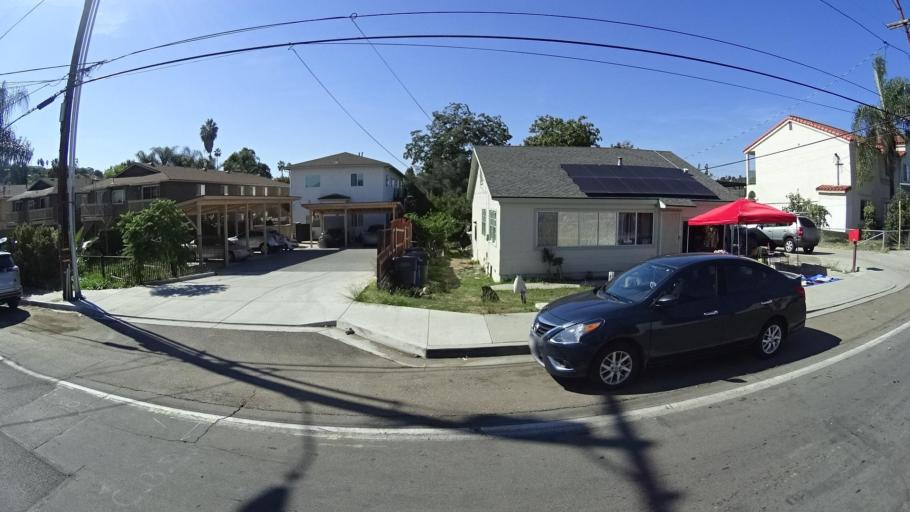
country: US
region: California
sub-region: San Diego County
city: Spring Valley
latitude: 32.7465
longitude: -116.9818
